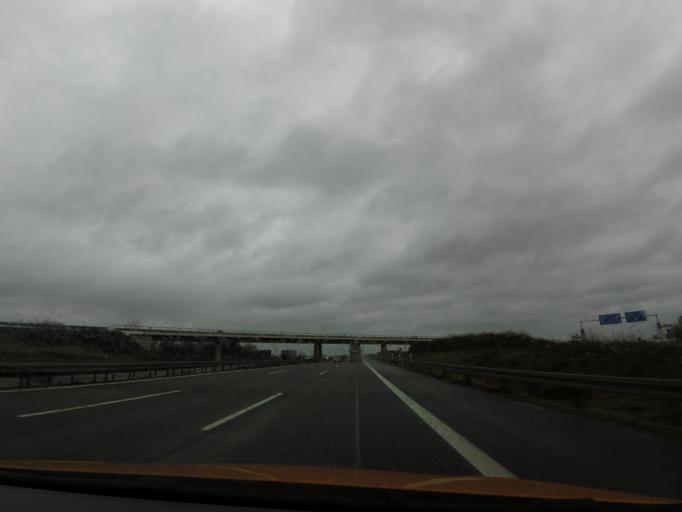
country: DE
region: Brandenburg
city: Schulzendorf
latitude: 52.3634
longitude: 13.5483
